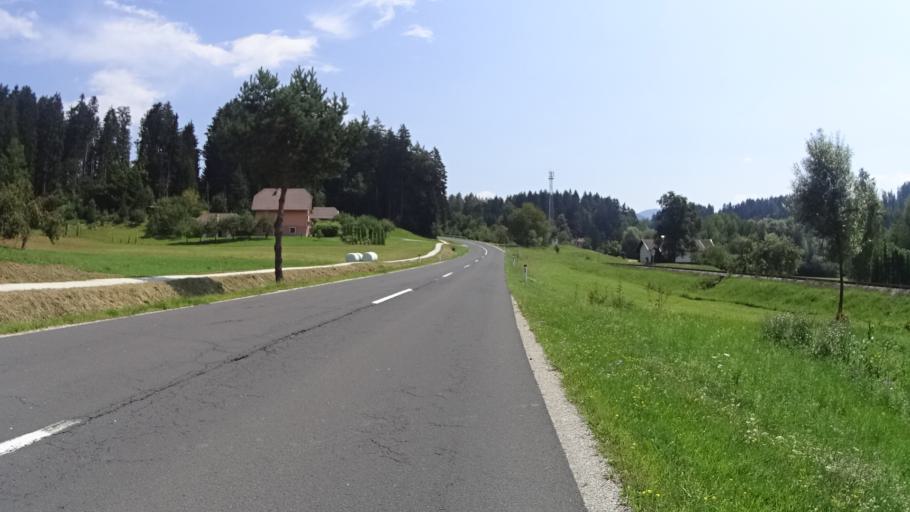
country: SI
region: Mezica
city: Mezica
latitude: 46.5655
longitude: 14.8437
